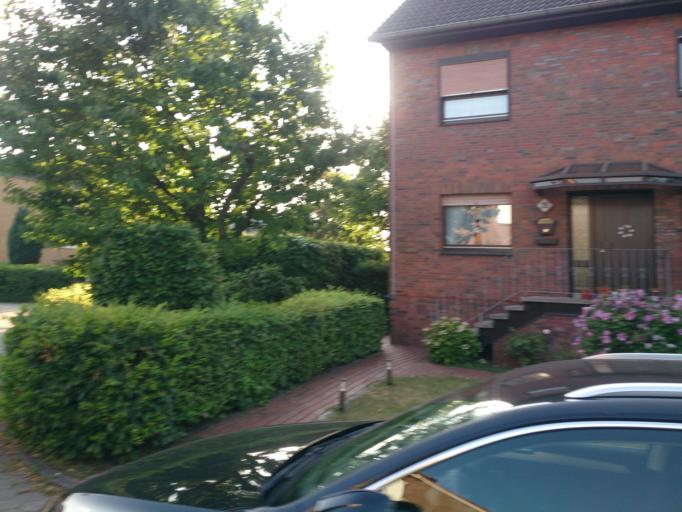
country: DE
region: Lower Saxony
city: Neu Wulmstorf
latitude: 53.5301
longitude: 9.8493
